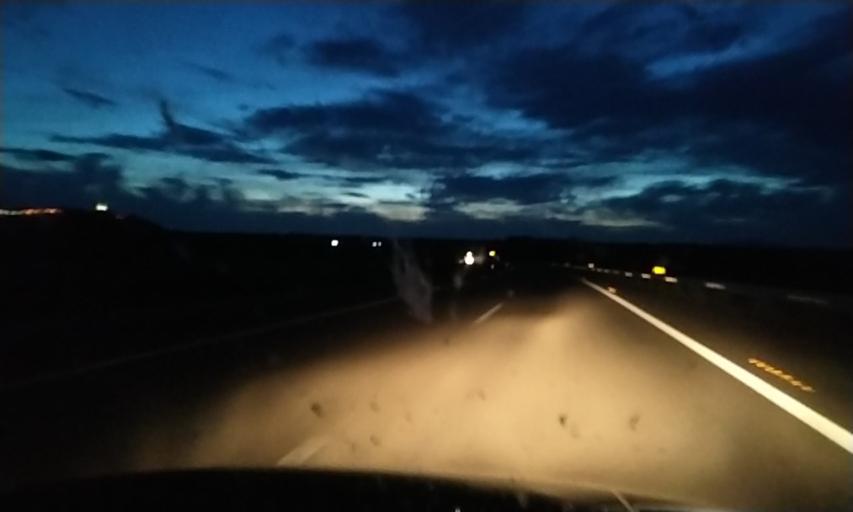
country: ES
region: Extremadura
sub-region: Provincia de Caceres
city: Galisteo
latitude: 39.9821
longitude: -6.2497
